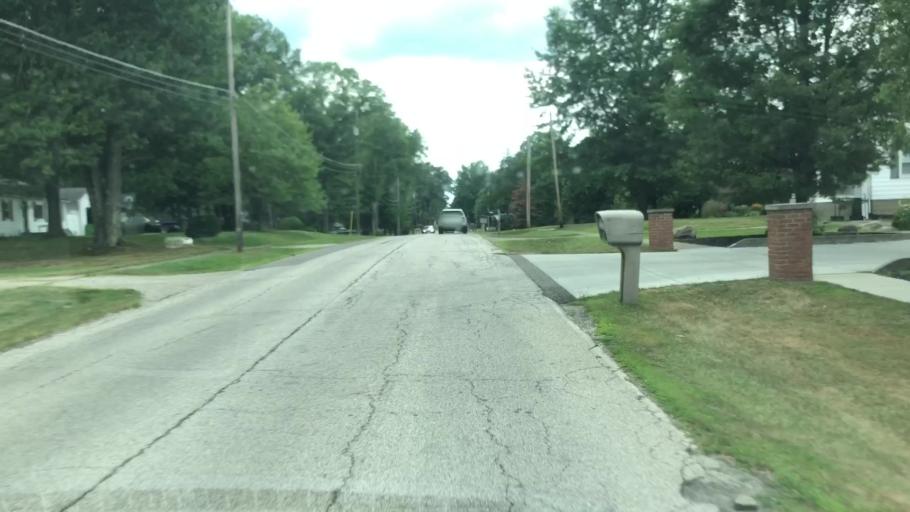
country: US
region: Ohio
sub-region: Summit County
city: Stow
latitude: 41.1825
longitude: -81.4280
